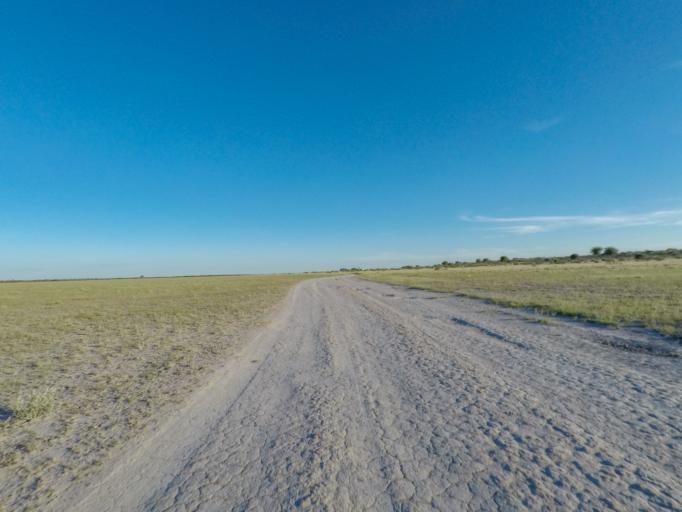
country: BW
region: Central
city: Rakops
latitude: -21.4007
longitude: 23.7951
